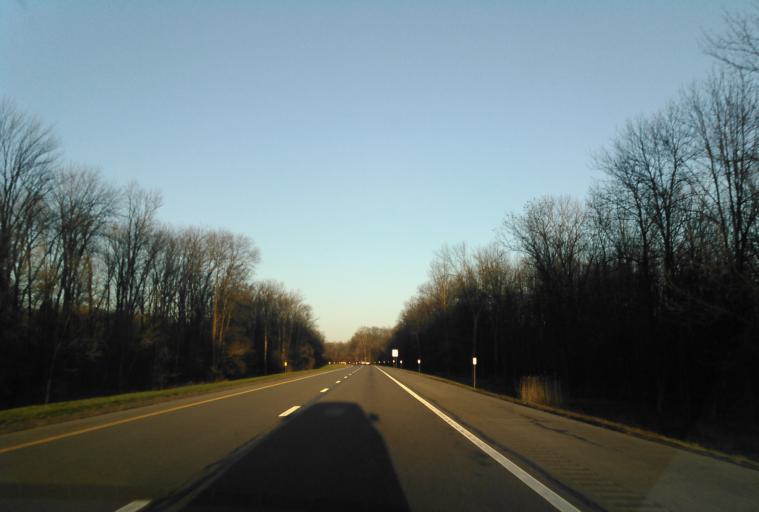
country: US
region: New York
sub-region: Ontario County
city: Manchester
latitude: 42.9760
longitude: -77.2102
